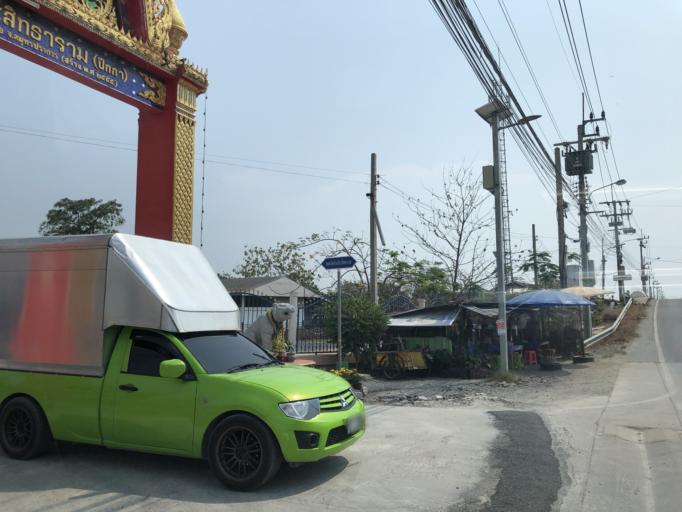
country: TH
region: Samut Prakan
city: Bang Bo
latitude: 13.5301
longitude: 100.8720
